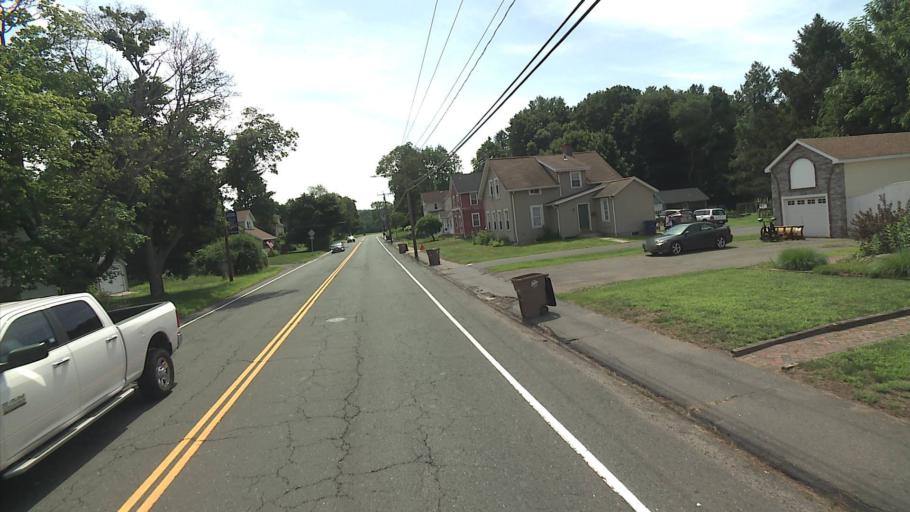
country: US
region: Connecticut
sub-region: Tolland County
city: Rockville
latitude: 41.8615
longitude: -72.4352
